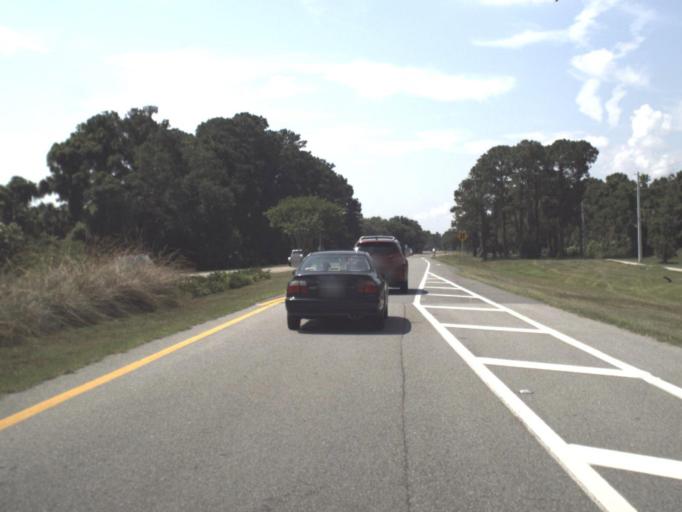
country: US
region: Florida
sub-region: Saint Johns County
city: Sawgrass
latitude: 30.1868
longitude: -81.3795
